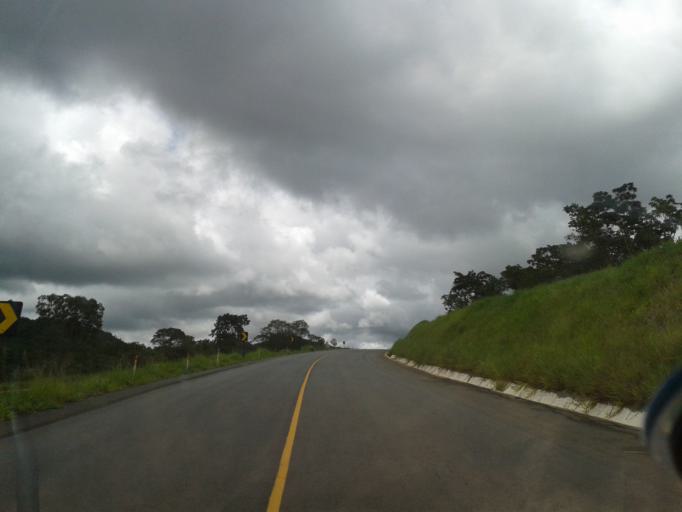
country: BR
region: Goias
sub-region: Goias
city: Goias
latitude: -16.0025
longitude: -50.0609
